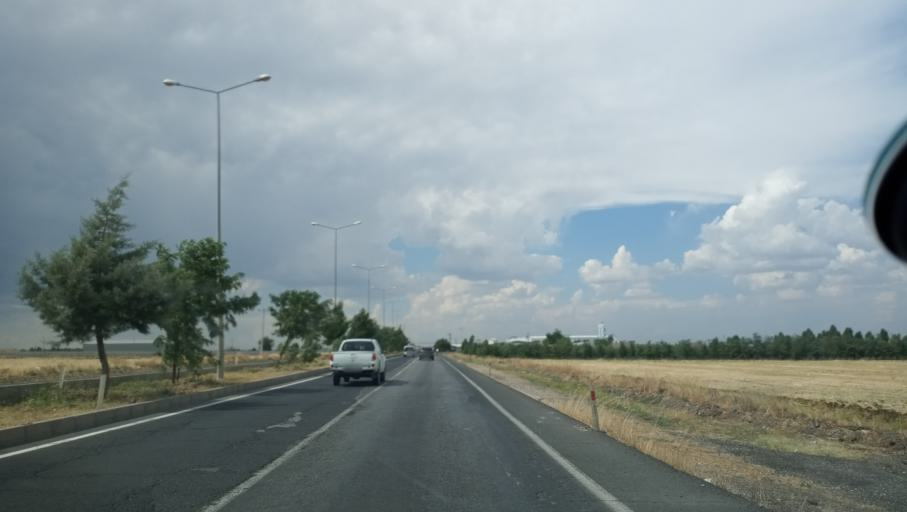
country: TR
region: Diyarbakir
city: Diyarbakir
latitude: 37.8792
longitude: 40.2203
